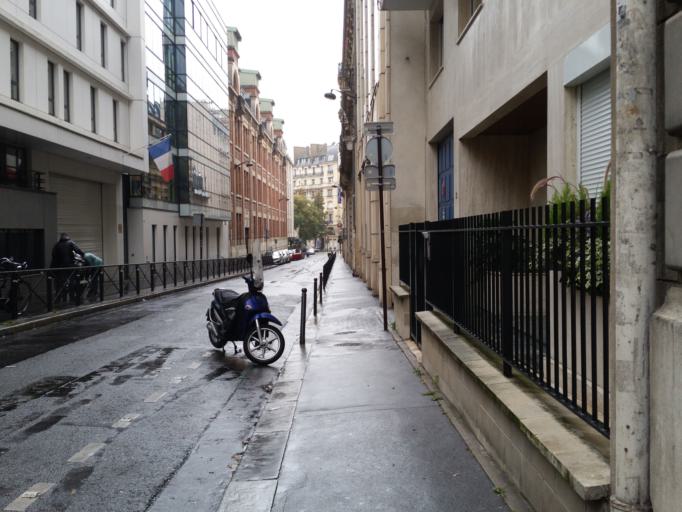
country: FR
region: Ile-de-France
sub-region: Paris
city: Paris
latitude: 48.8441
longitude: 2.3273
